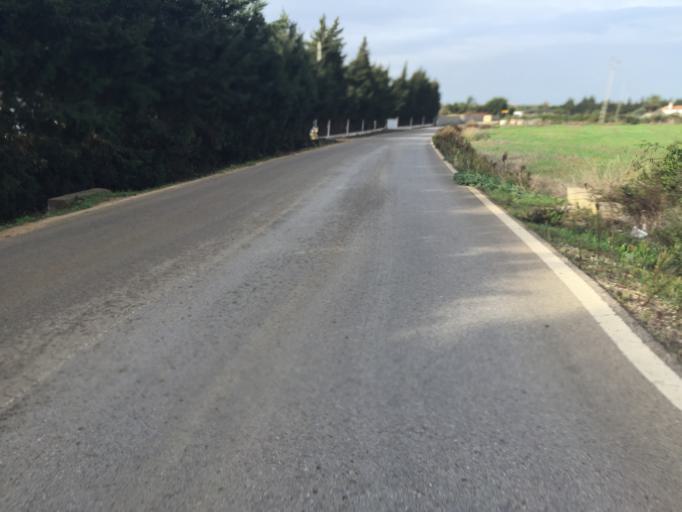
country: ES
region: Andalusia
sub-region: Provincia de Cadiz
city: Conil de la Frontera
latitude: 36.3025
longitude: -6.1152
